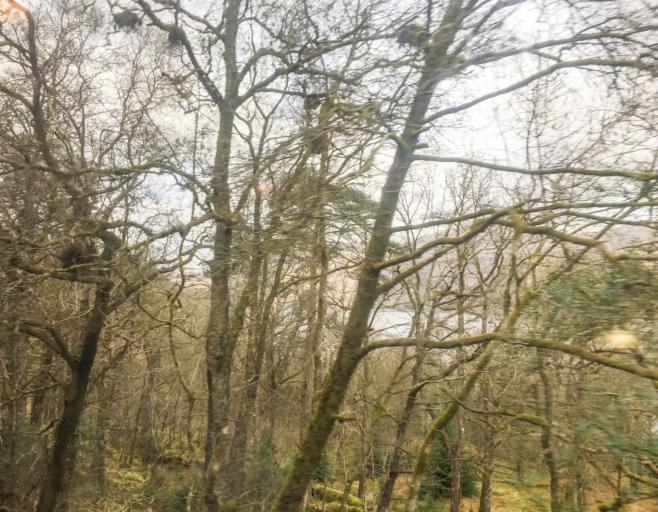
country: GB
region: Scotland
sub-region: Argyll and Bute
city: Garelochhead
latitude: 56.2407
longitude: -4.7116
